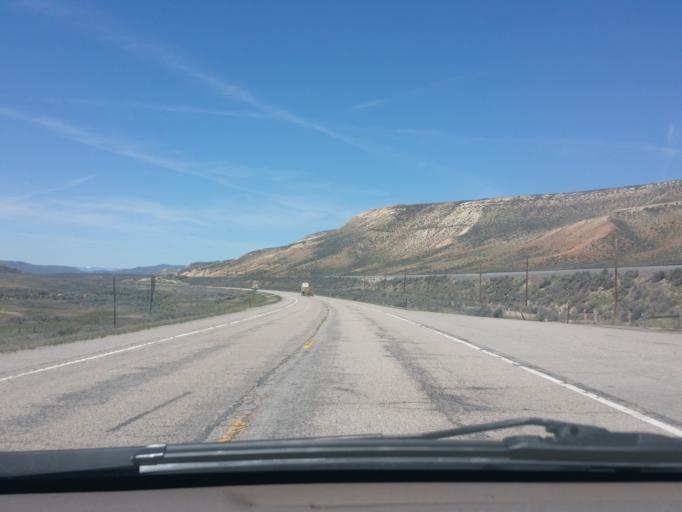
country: US
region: Wyoming
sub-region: Lincoln County
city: Kemmerer
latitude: 41.8149
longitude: -110.6296
